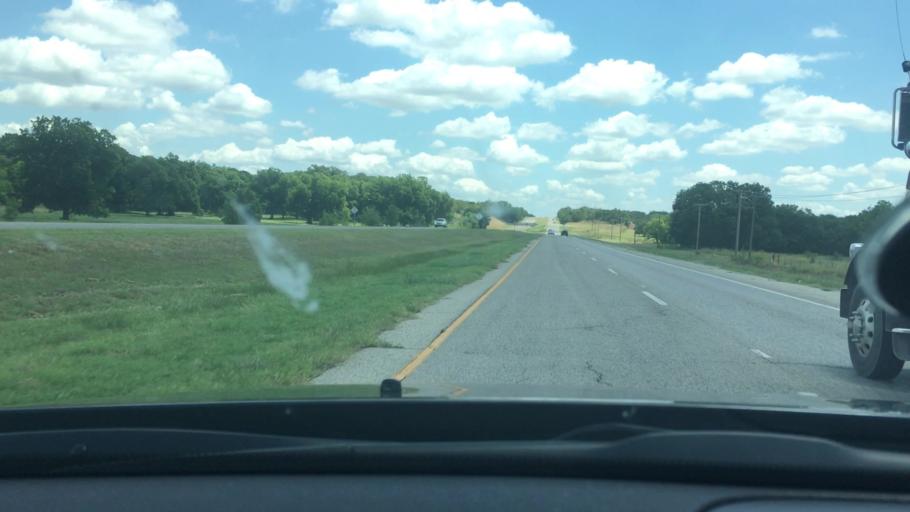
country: US
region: Oklahoma
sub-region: Carter County
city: Wilson
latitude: 34.1728
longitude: -97.3594
